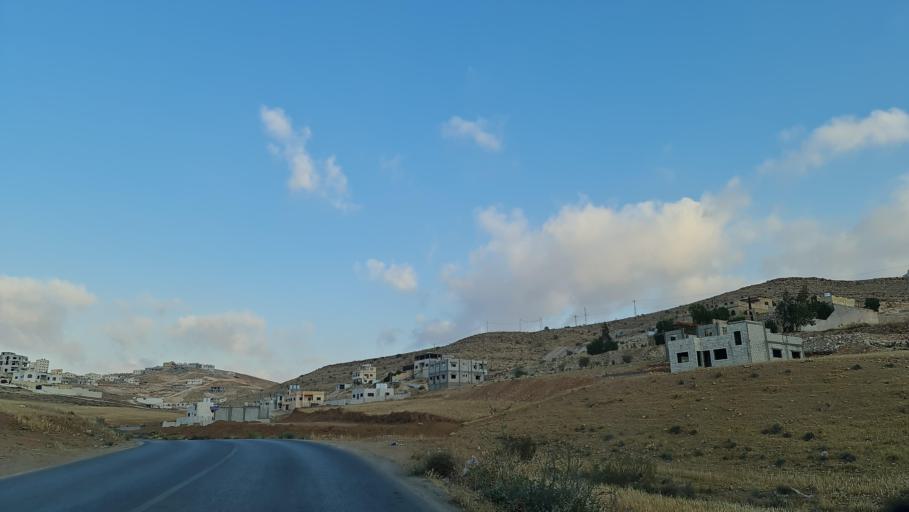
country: JO
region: Zarqa
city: Zarqa
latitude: 32.0820
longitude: 36.0426
